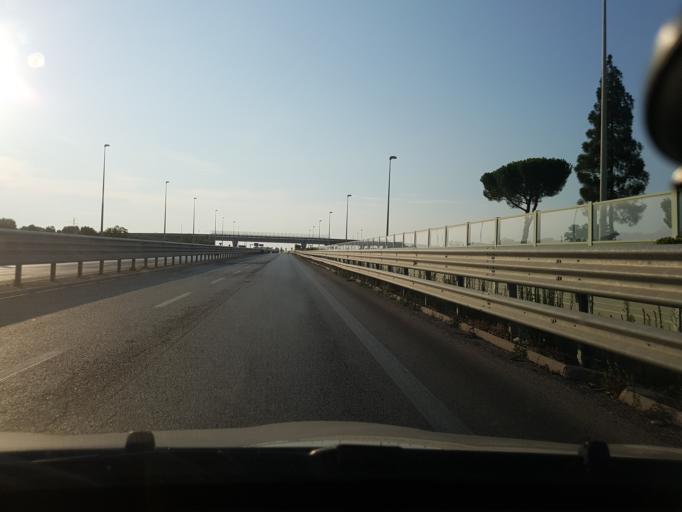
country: IT
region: Apulia
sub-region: Provincia di Foggia
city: Stornara
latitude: 41.3091
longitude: 15.8045
